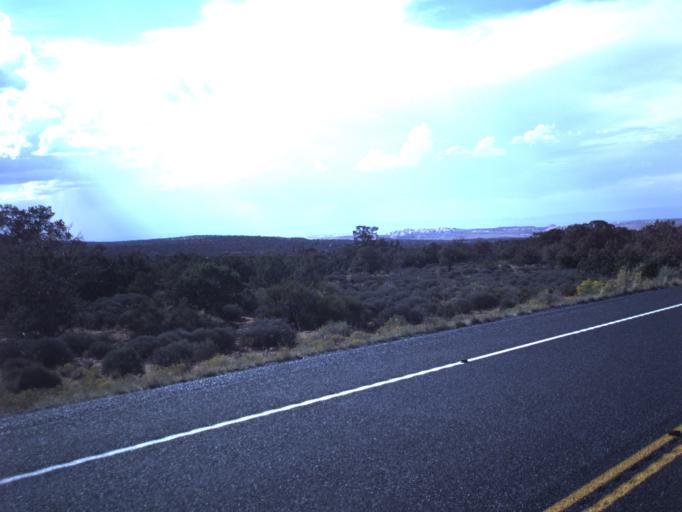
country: US
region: Utah
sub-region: Grand County
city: Moab
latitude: 38.5879
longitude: -109.8065
